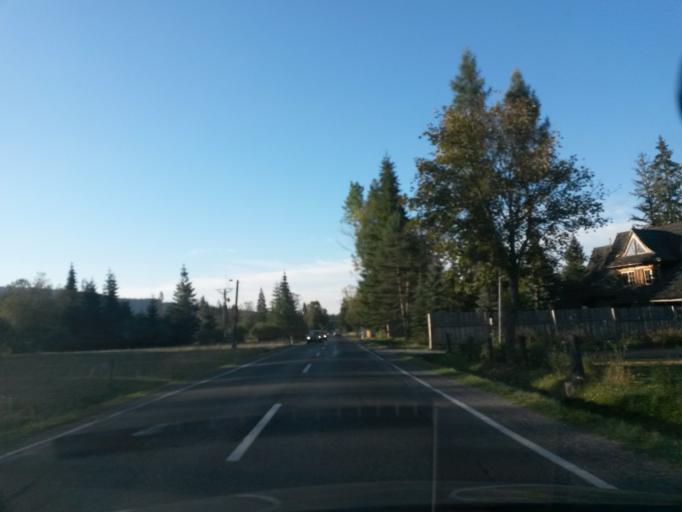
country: PL
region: Lesser Poland Voivodeship
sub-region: Powiat tatrzanski
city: Koscielisko
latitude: 49.2861
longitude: 19.8537
